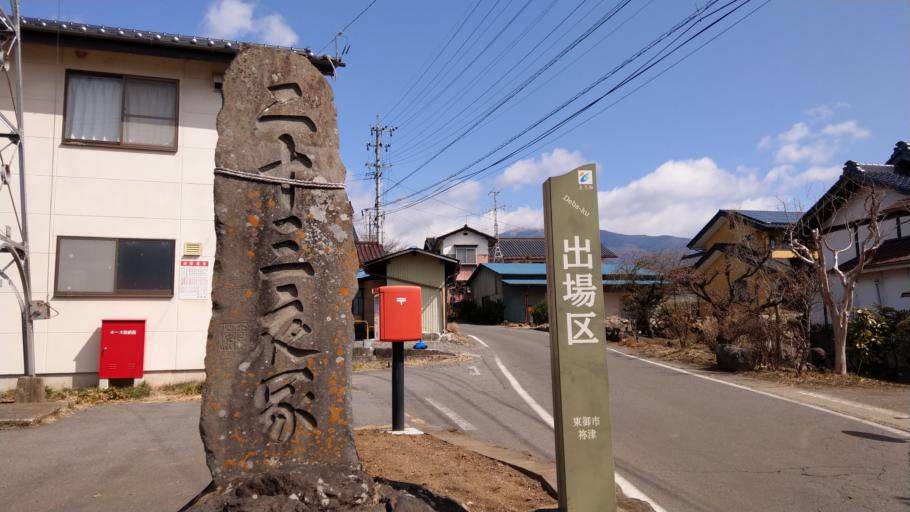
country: JP
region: Nagano
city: Komoro
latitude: 36.3652
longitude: 138.3634
